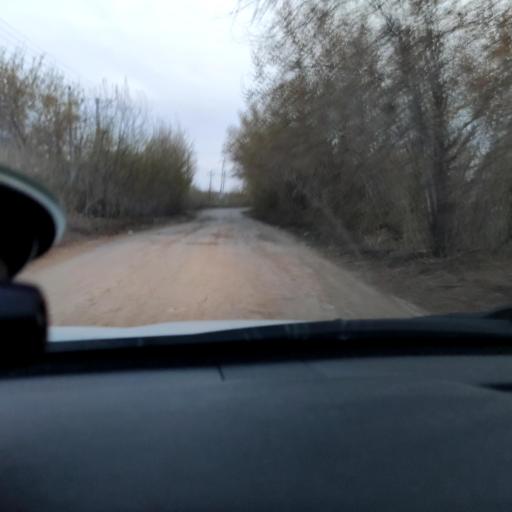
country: RU
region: Samara
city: Smyshlyayevka
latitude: 53.1524
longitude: 50.3903
